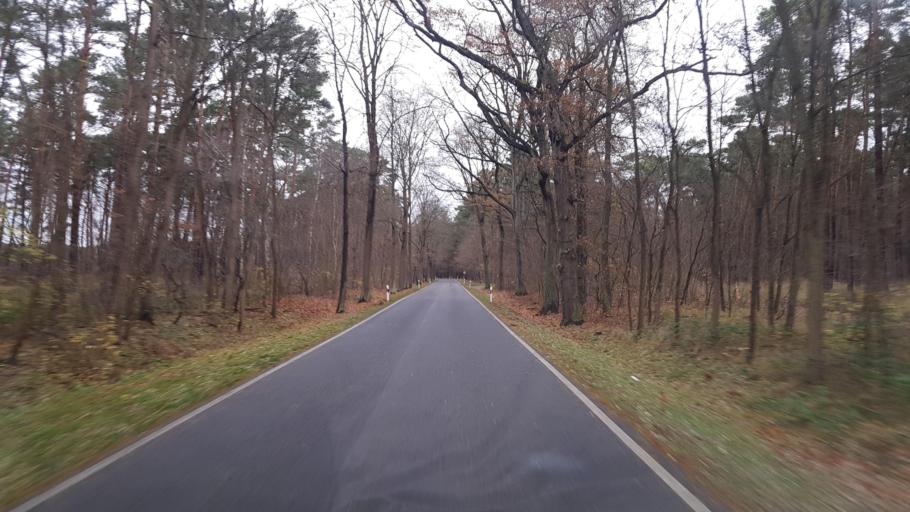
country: DE
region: Brandenburg
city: Tauche
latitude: 52.0944
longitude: 14.1674
